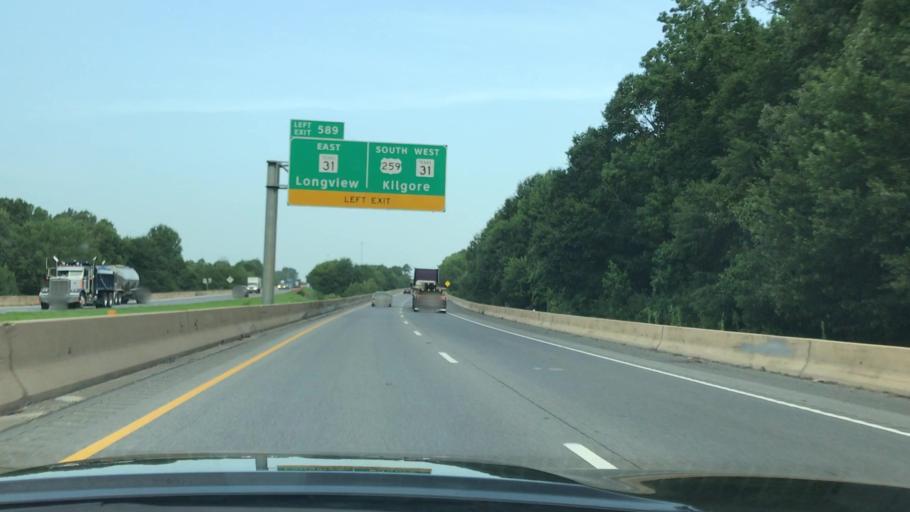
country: US
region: Texas
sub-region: Gregg County
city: Kilgore
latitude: 32.4351
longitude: -94.8179
